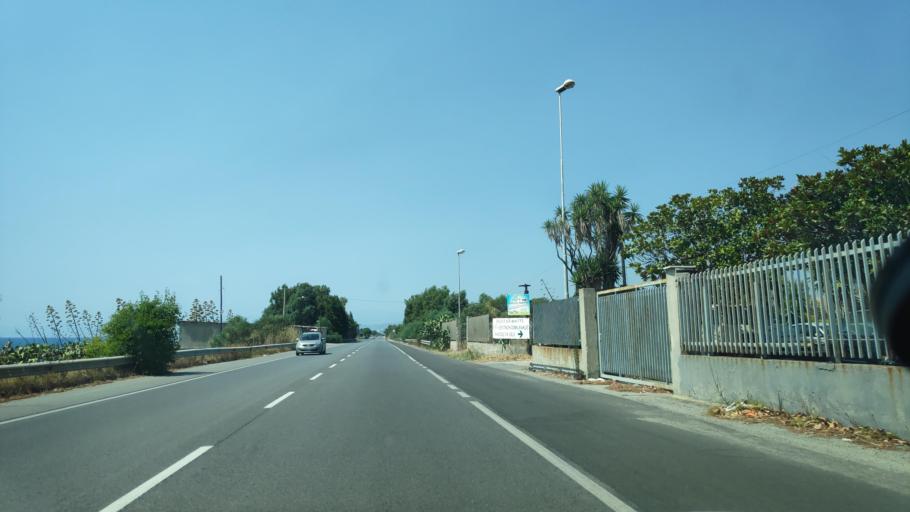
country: IT
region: Calabria
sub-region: Provincia di Reggio Calabria
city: Roccella Ionica
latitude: 38.3113
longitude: 16.3748
